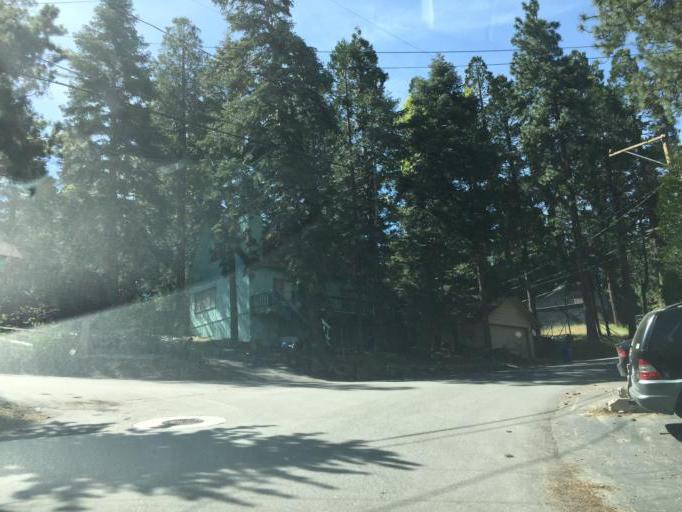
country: US
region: California
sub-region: San Bernardino County
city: Lake Arrowhead
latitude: 34.2412
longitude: -117.2321
